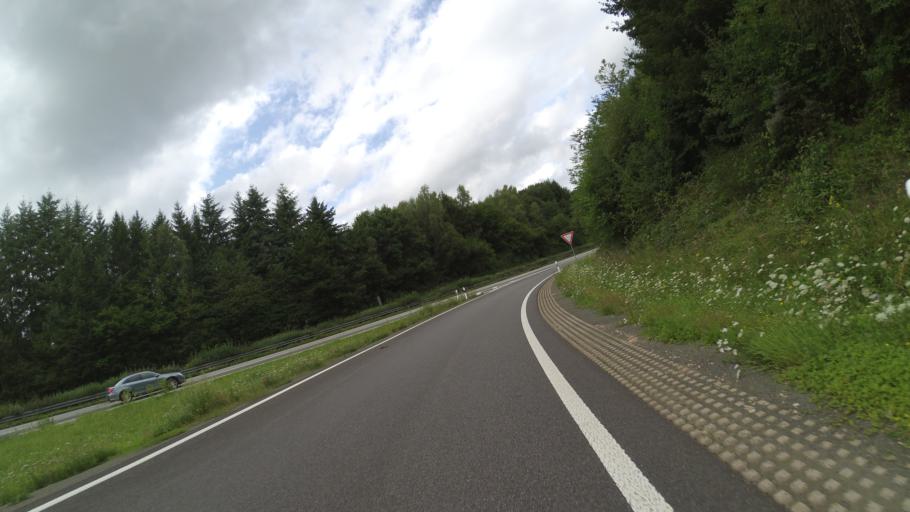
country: DE
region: Saarland
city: Tholey
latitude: 49.4907
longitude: 6.9878
